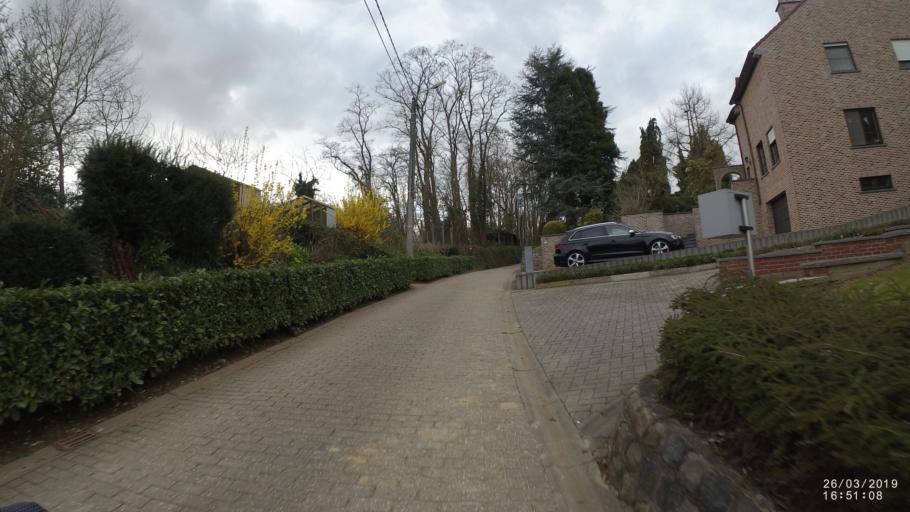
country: BE
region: Flanders
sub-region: Provincie Vlaams-Brabant
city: Bertem
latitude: 50.8390
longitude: 4.6369
